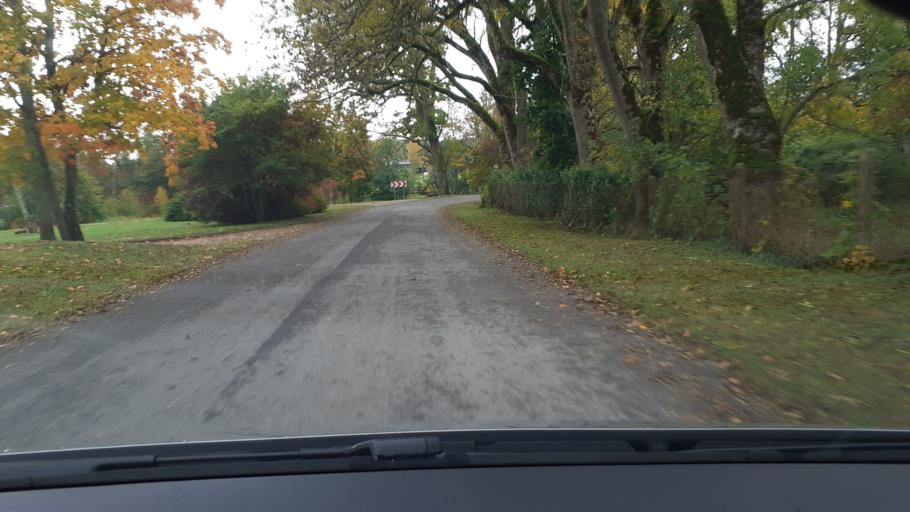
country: LV
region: Kuldigas Rajons
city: Kuldiga
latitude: 57.0194
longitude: 21.9136
